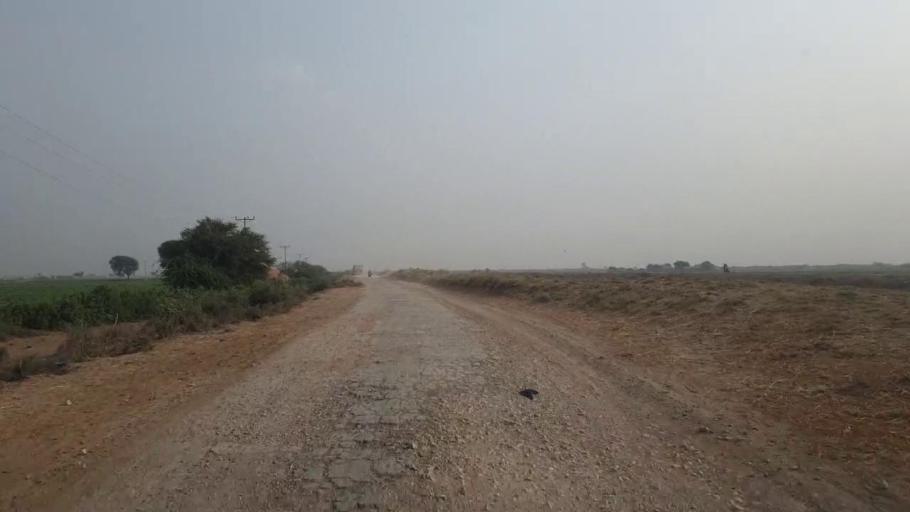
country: PK
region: Sindh
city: Mirpur Batoro
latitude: 24.5700
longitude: 68.3985
